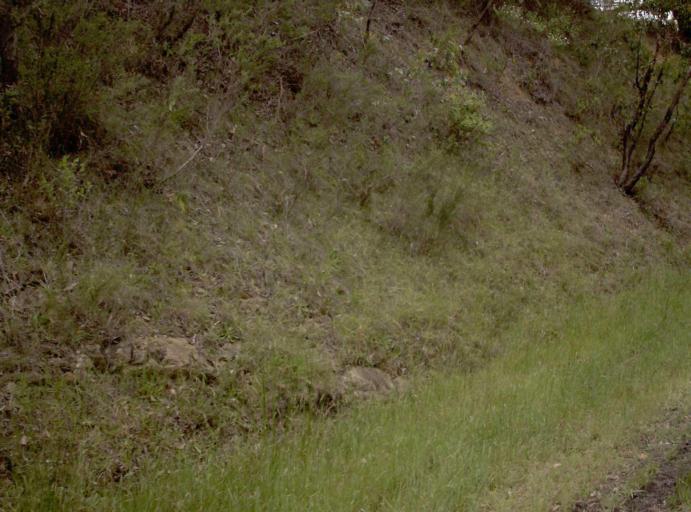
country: AU
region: Victoria
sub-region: Bass Coast
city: North Wonthaggi
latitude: -38.5247
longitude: 145.7005
